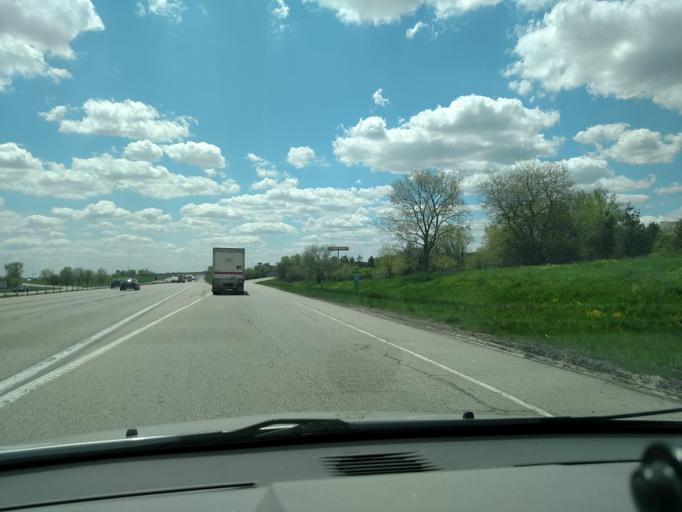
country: US
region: Iowa
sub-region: Polk County
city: Ankeny
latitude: 41.7081
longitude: -93.5765
